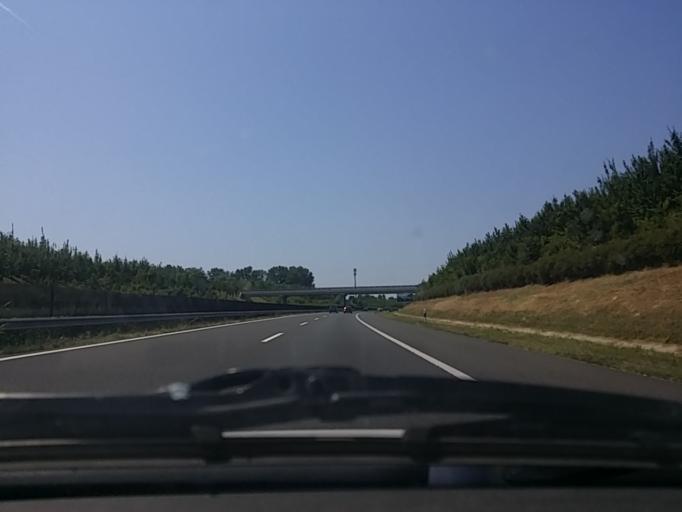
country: HU
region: Somogy
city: Balatonlelle
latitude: 46.7686
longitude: 17.7116
